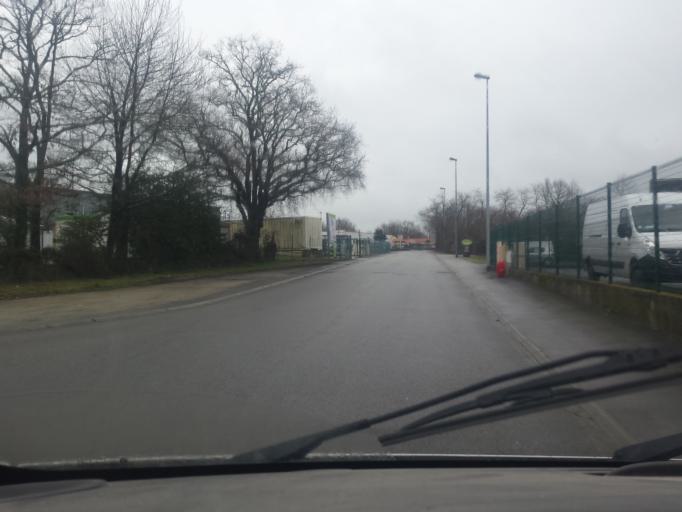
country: FR
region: Pays de la Loire
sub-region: Departement de la Vendee
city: La Roche-sur-Yon
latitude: 46.6412
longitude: -1.4130
